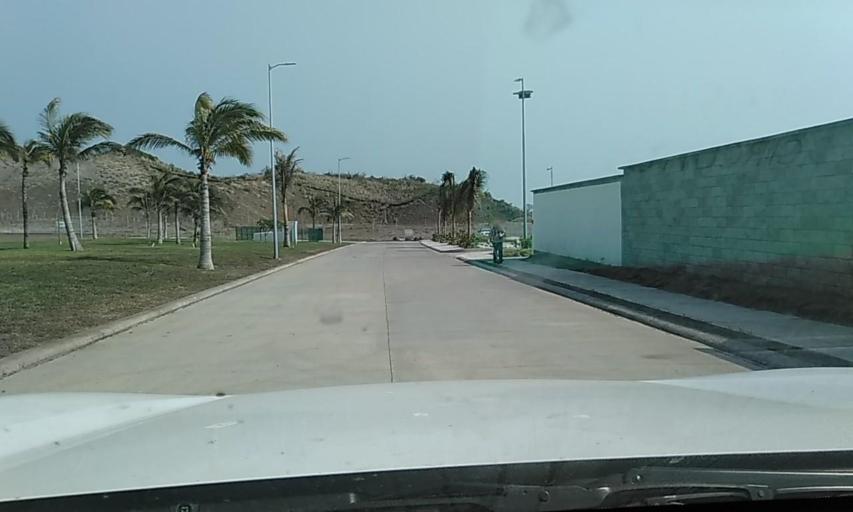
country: MX
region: Veracruz
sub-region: Alvarado
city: Playa de la Libertad
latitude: 19.0413
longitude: -96.0605
